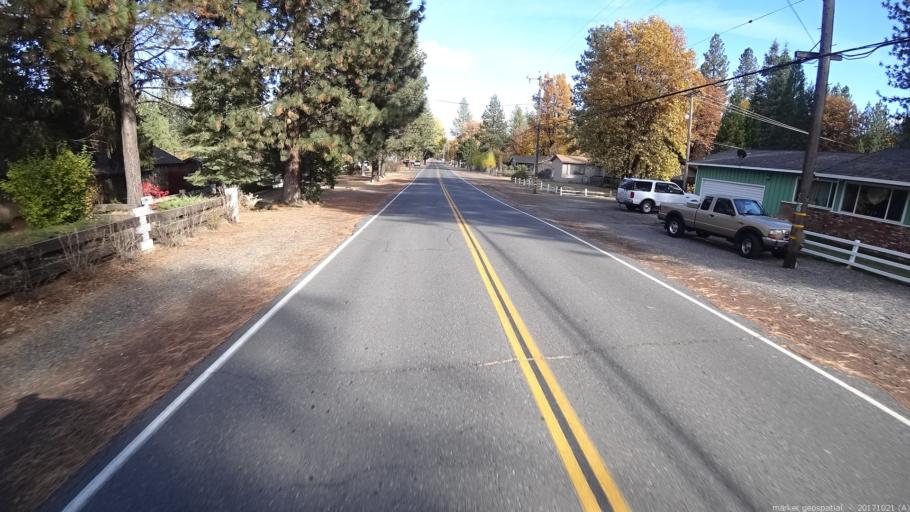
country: US
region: California
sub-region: Shasta County
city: Burney
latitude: 40.8761
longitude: -121.6692
